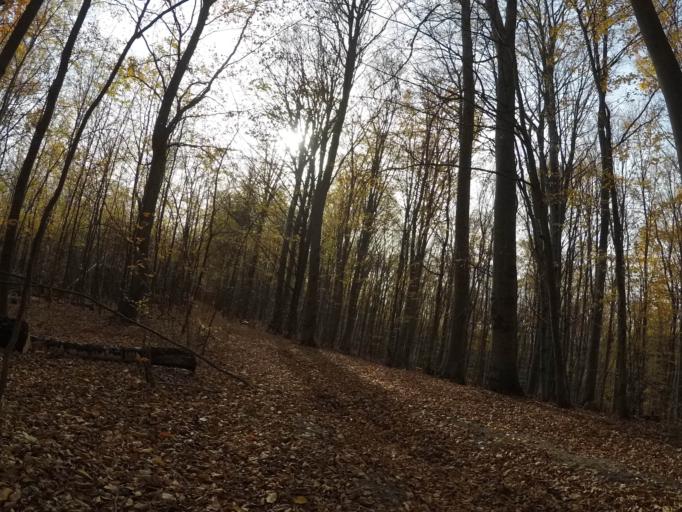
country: SK
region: Presovsky
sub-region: Okres Presov
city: Presov
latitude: 48.9546
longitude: 21.1859
